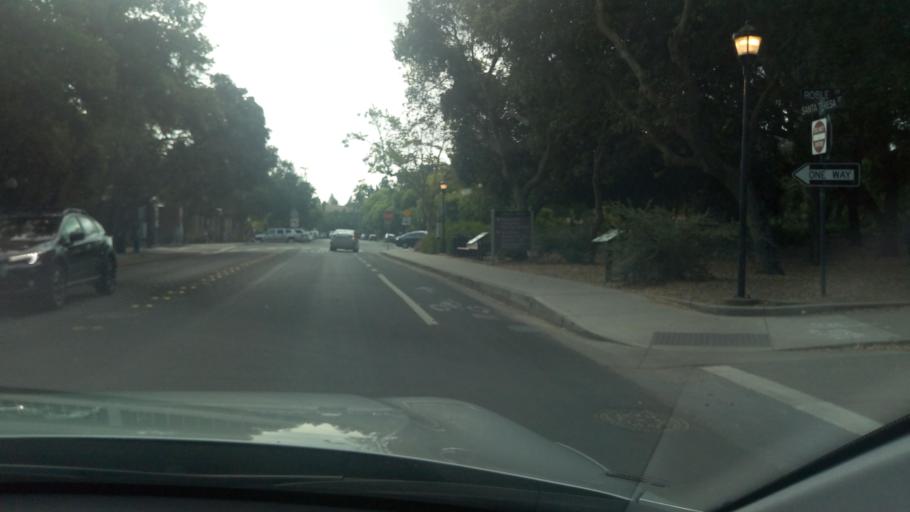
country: US
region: California
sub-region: Santa Clara County
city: Stanford
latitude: 37.4253
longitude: -122.1738
